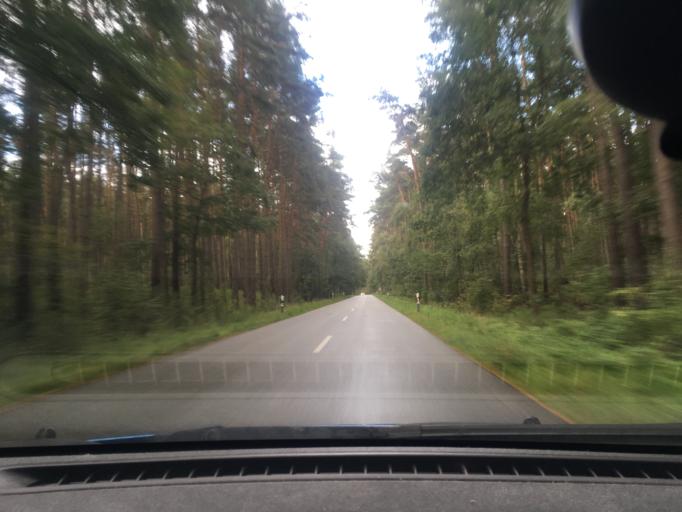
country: DE
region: Lower Saxony
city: Neu Darchau
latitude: 53.3138
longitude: 10.9112
